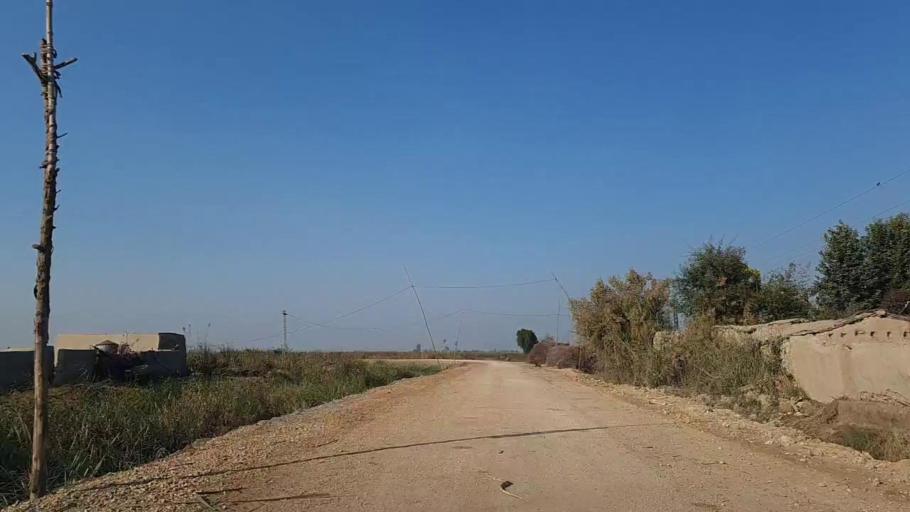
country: PK
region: Sindh
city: Bandhi
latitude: 26.6064
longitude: 68.3132
